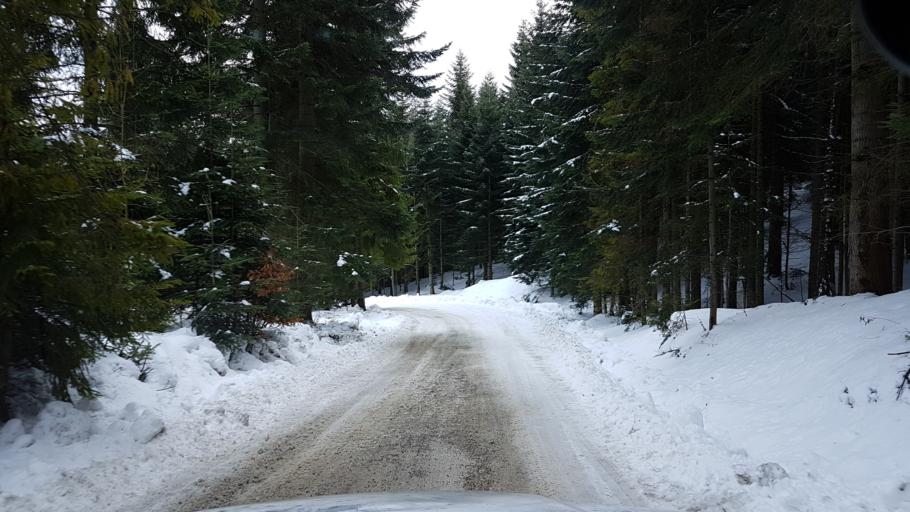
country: PL
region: Lesser Poland Voivodeship
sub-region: Powiat nowosadecki
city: Rytro
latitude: 49.4192
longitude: 20.6287
